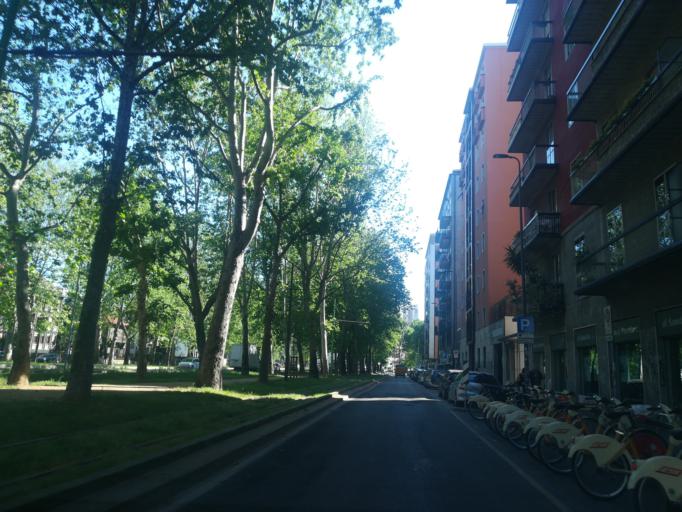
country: IT
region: Lombardy
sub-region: Citta metropolitana di Milano
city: Milano
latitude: 45.4916
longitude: 9.1919
